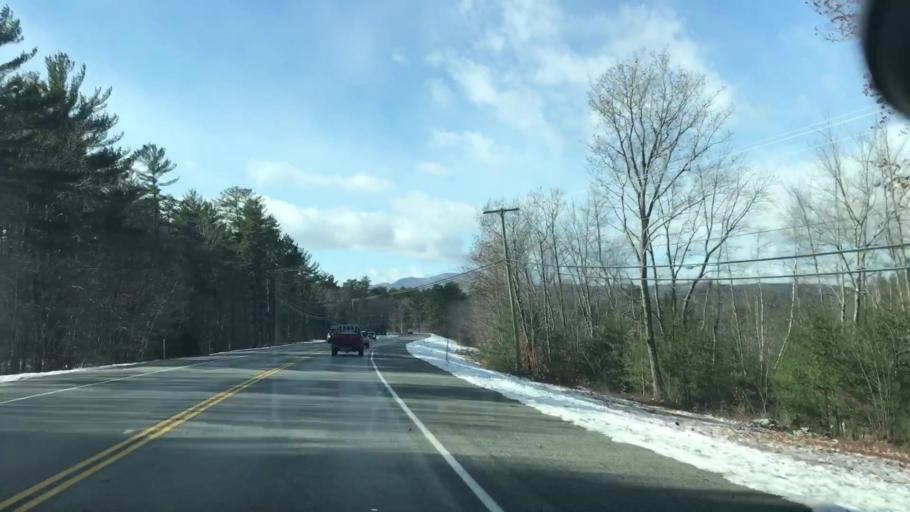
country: US
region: New Hampshire
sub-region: Carroll County
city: Ossipee
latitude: 43.7642
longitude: -71.1274
